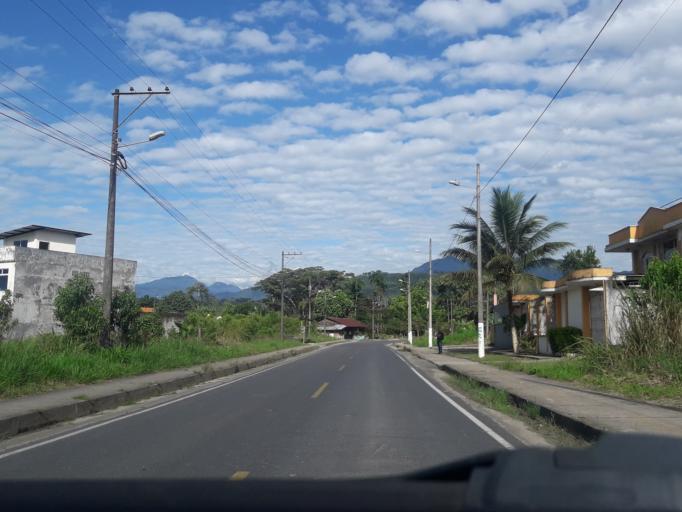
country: EC
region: Napo
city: Tena
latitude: -0.9865
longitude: -77.8336
